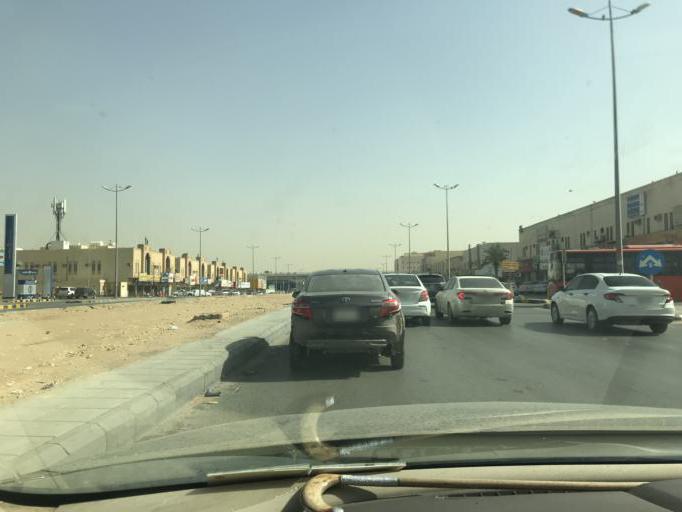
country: SA
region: Ar Riyad
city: Riyadh
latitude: 24.7959
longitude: 46.7423
